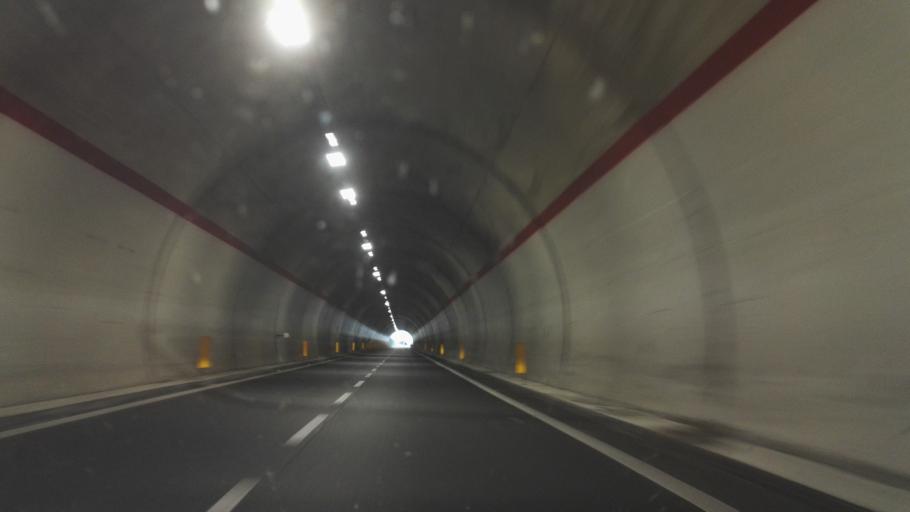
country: IT
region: Calabria
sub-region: Provincia di Reggio Calabria
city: Roccella Ionica
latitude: 38.3292
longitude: 16.4025
